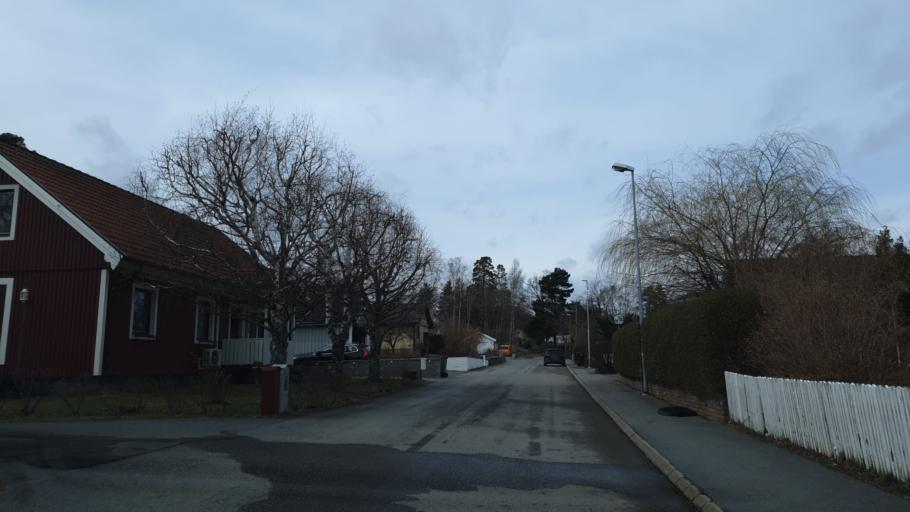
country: SE
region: Stockholm
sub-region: Nacka Kommun
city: Boo
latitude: 59.3289
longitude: 18.2757
